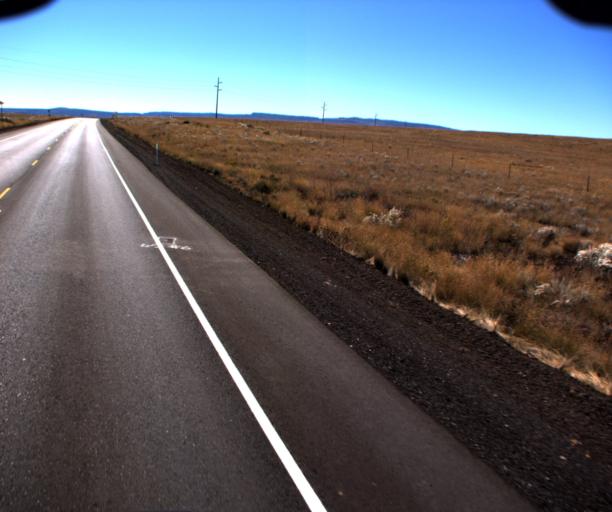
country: US
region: Arizona
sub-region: Apache County
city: Springerville
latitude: 34.1855
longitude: -109.3196
